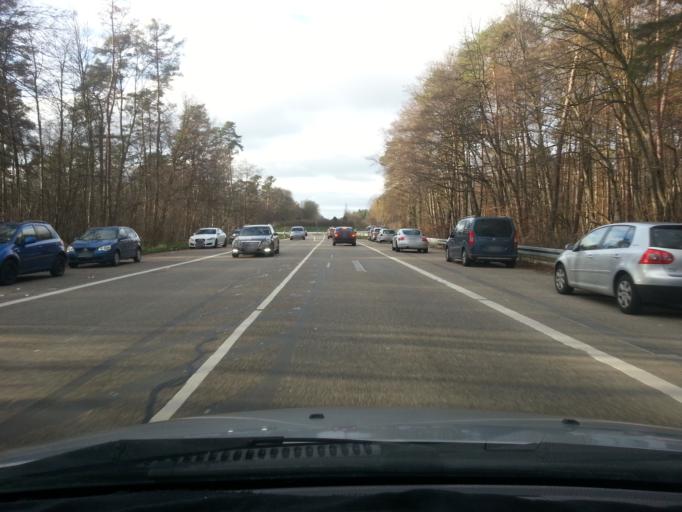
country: DE
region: Baden-Wuerttemberg
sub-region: Karlsruhe Region
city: Kronau
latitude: 49.2254
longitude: 8.6088
